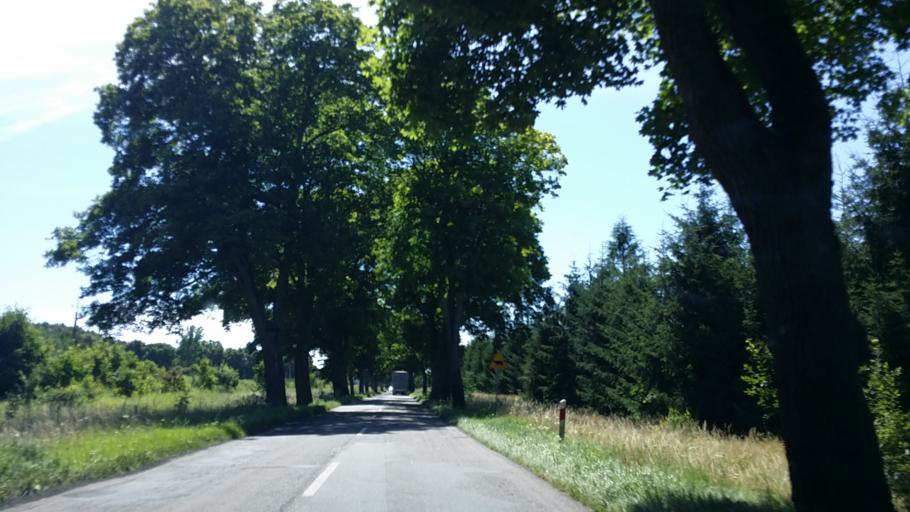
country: PL
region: West Pomeranian Voivodeship
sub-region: Powiat lobeski
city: Lobez
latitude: 53.6526
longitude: 15.6432
